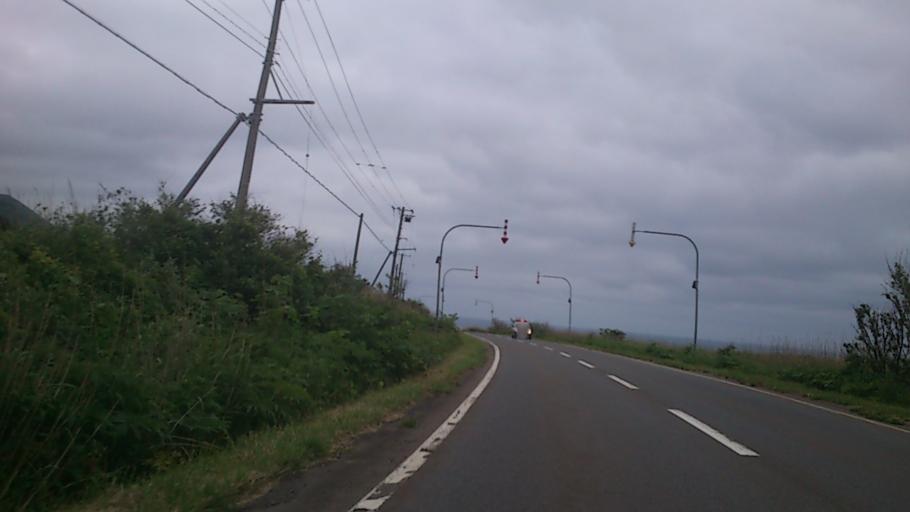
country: JP
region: Hokkaido
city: Kamiiso
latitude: 41.7173
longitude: 140.0326
